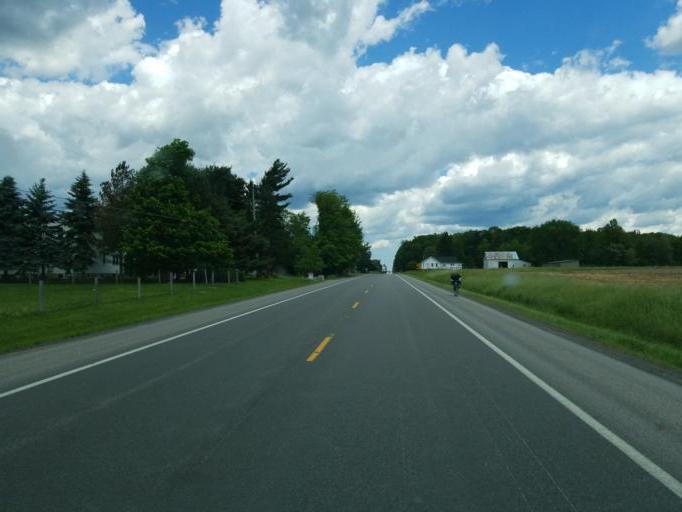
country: US
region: Ohio
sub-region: Geauga County
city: Middlefield
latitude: 41.4079
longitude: -81.0602
